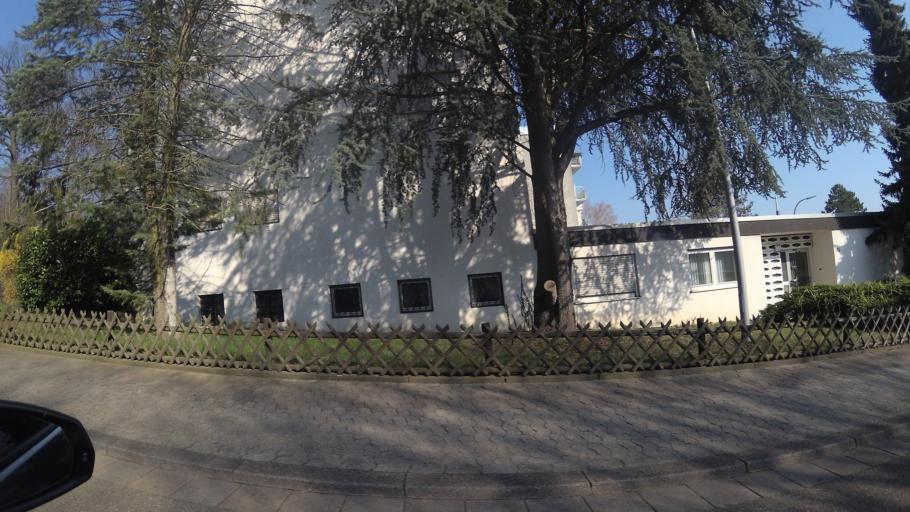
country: DE
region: Saarland
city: Saarbrucken
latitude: 49.2508
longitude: 6.9963
